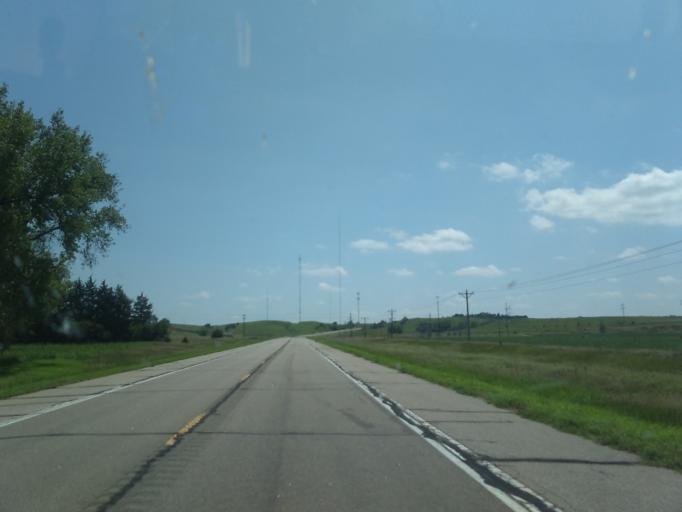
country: US
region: Nebraska
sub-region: Dawson County
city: Lexington
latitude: 40.7109
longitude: -99.7873
